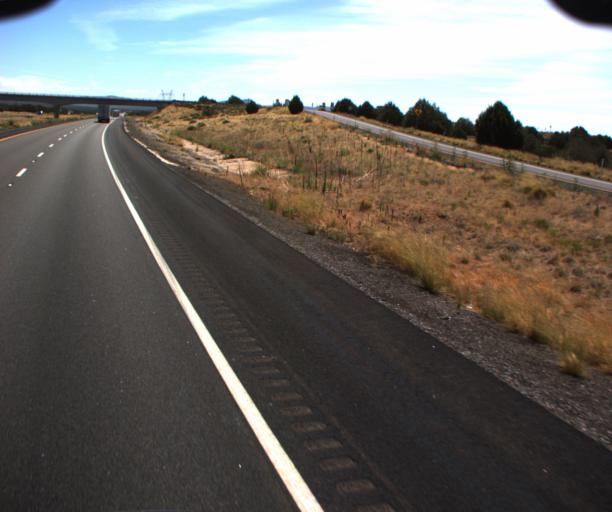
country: US
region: Arizona
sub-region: Mohave County
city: Peach Springs
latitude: 35.1906
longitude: -113.3678
